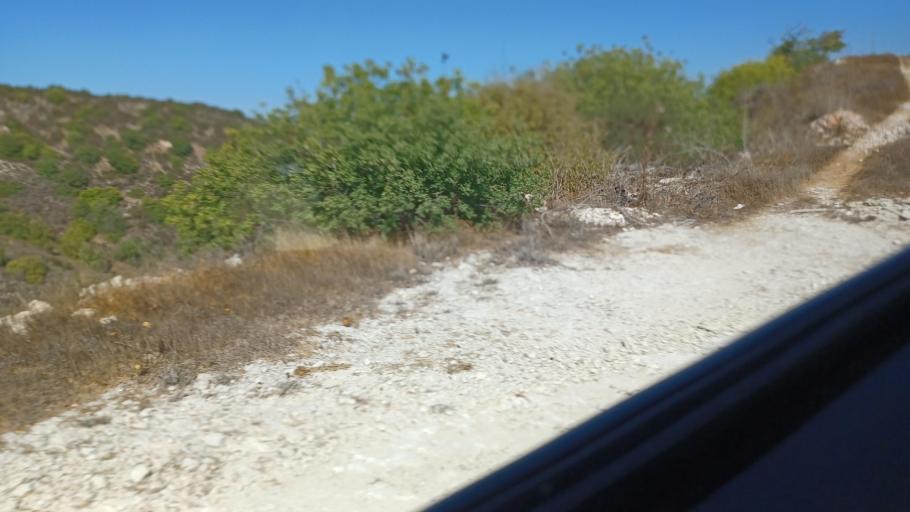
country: CY
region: Pafos
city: Tala
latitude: 34.8651
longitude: 32.4489
